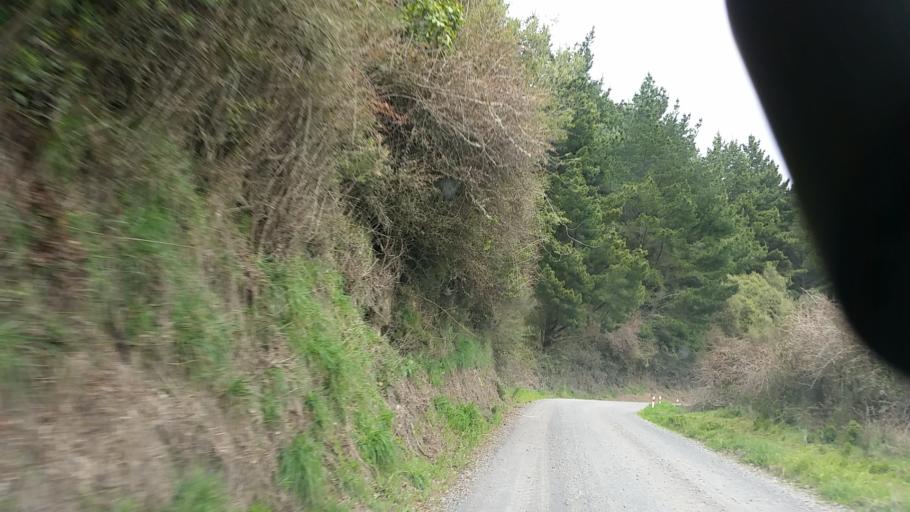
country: NZ
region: Bay of Plenty
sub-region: Rotorua District
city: Rotorua
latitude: -38.3866
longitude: 176.1719
